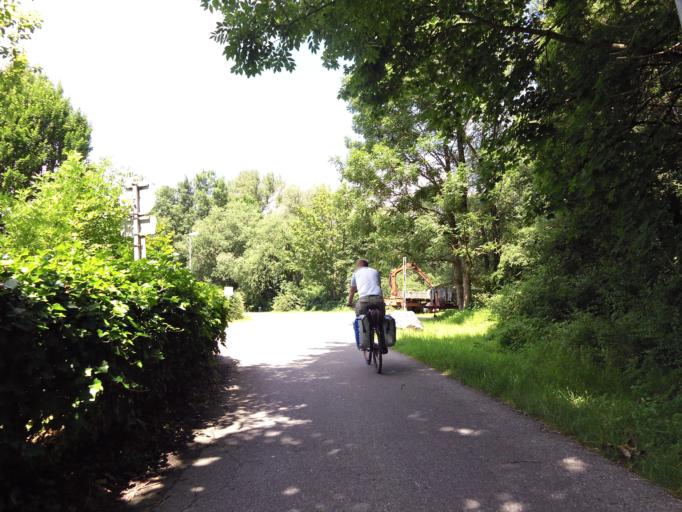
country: AT
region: Vorarlberg
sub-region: Politischer Bezirk Bregenz
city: Hard
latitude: 47.4994
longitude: 9.6979
